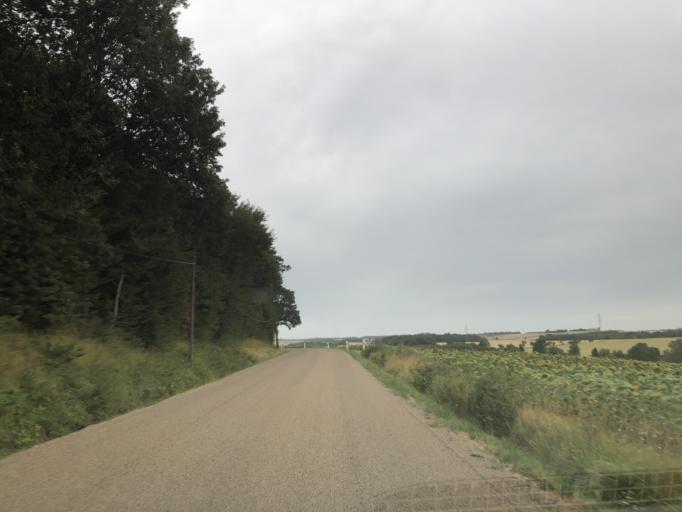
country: FR
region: Bourgogne
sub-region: Departement de l'Yonne
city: Charny
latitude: 47.9591
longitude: 3.1389
